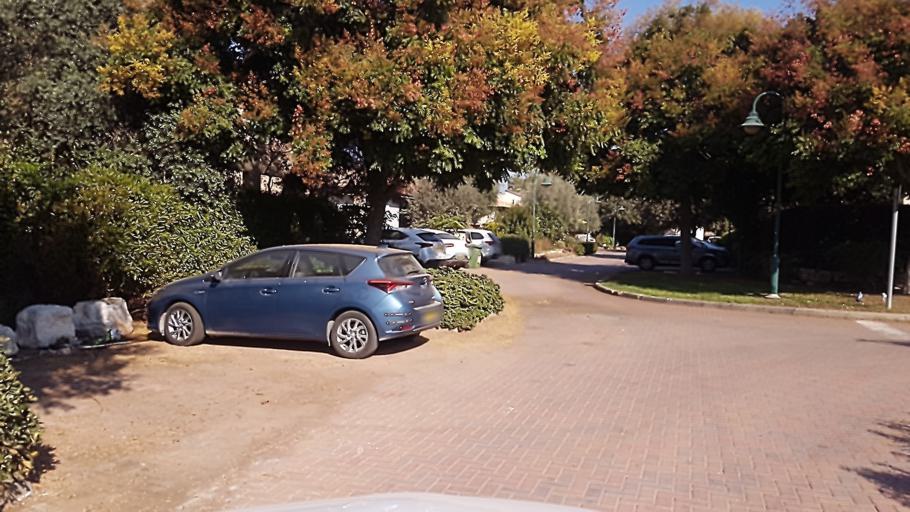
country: IL
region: Central District
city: Ra'anana
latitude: 32.2137
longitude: 34.8953
